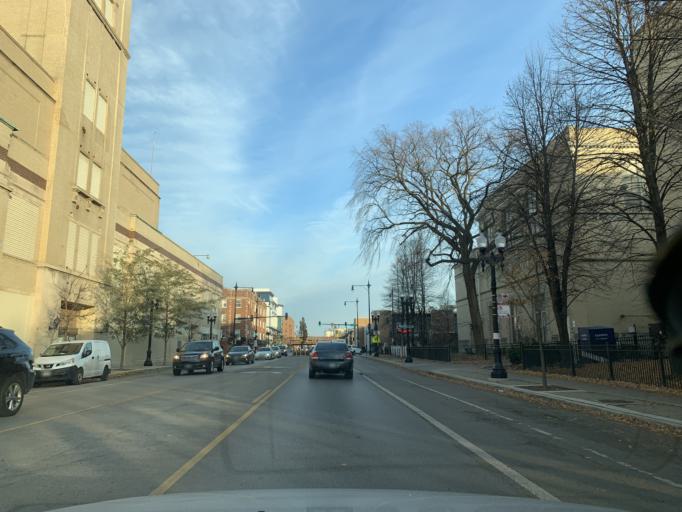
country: US
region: Illinois
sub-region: Cook County
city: Lincolnwood
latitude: 41.9688
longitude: -87.6773
